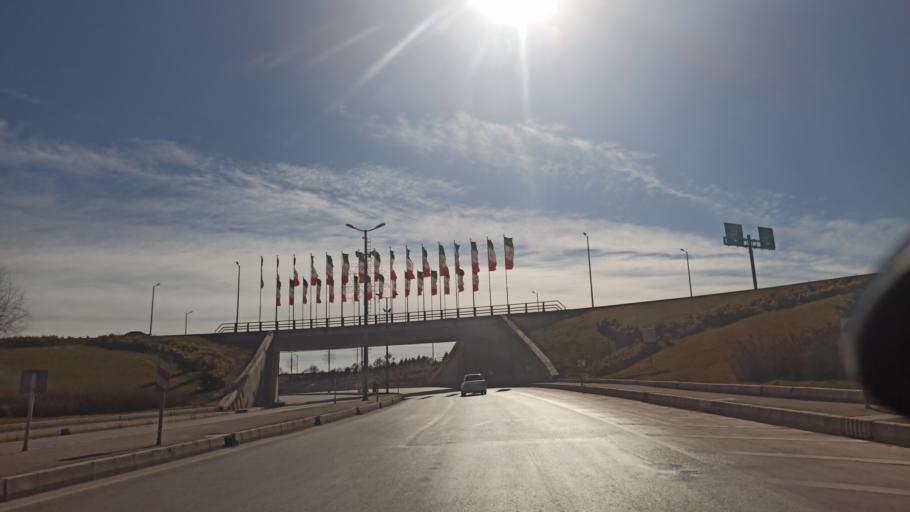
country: IR
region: Qazvin
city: Qazvin
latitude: 36.2451
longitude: 50.0014
